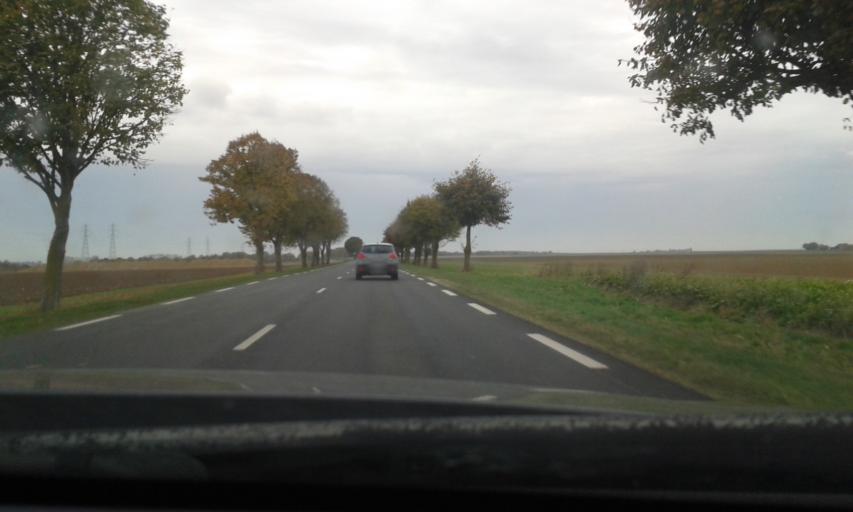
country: FR
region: Centre
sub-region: Departement du Loiret
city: Artenay
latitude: 48.1190
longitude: 1.8585
